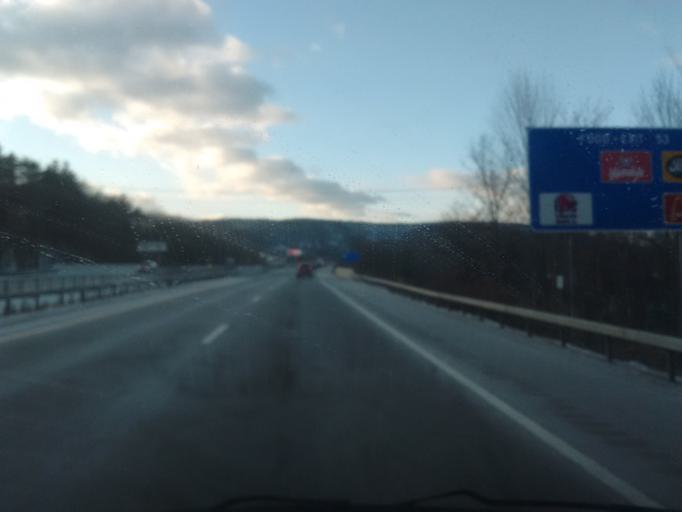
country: US
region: Pennsylvania
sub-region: Pike County
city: Matamoras
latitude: 41.3560
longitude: -74.6899
